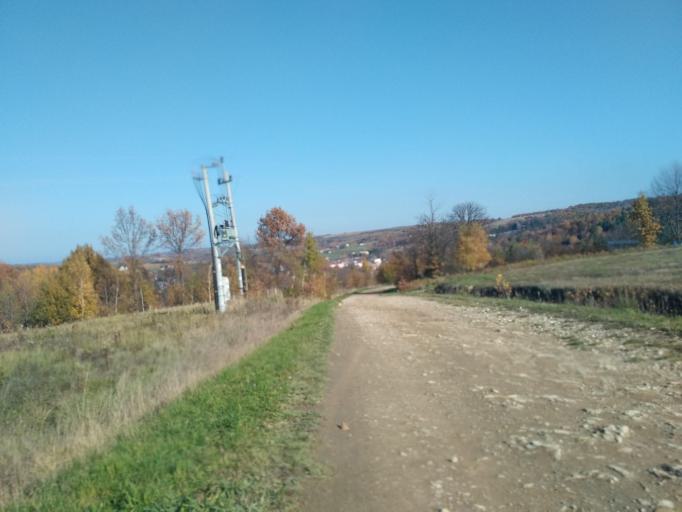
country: PL
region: Subcarpathian Voivodeship
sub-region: Powiat rzeszowski
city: Blazowa
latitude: 49.8750
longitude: 22.0911
